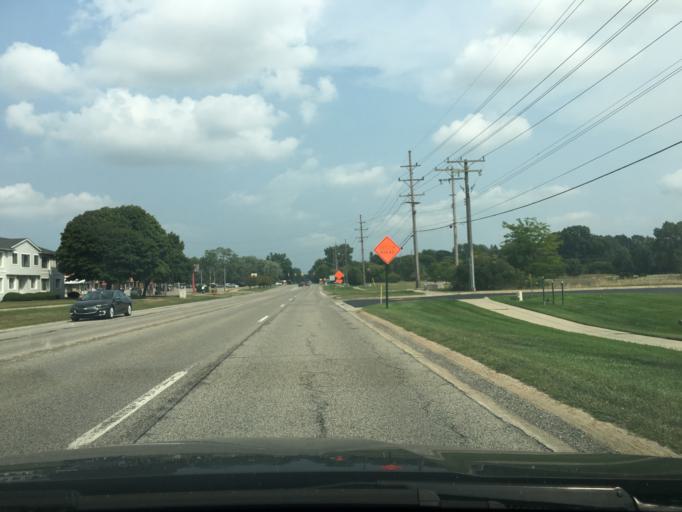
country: US
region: Michigan
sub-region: Oakland County
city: Bloomfield Hills
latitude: 42.6205
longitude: -83.2278
